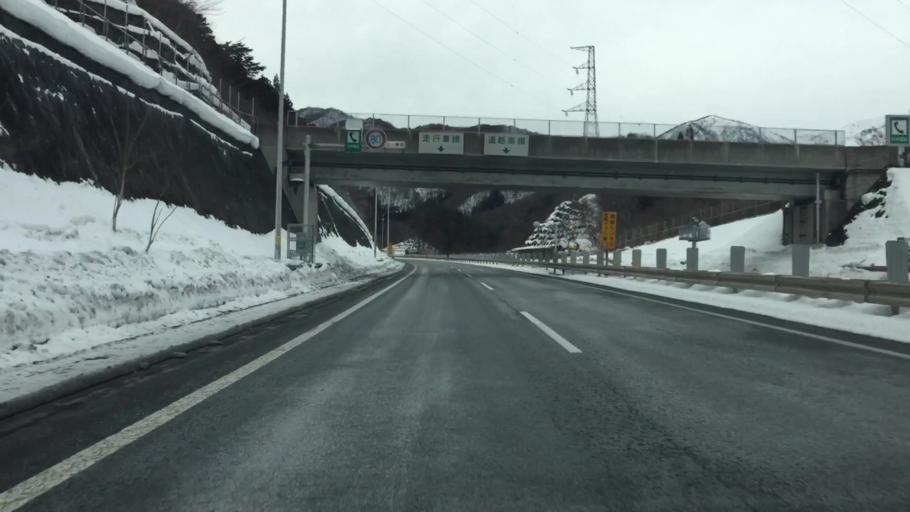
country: JP
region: Gunma
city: Numata
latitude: 36.7675
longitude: 138.9629
